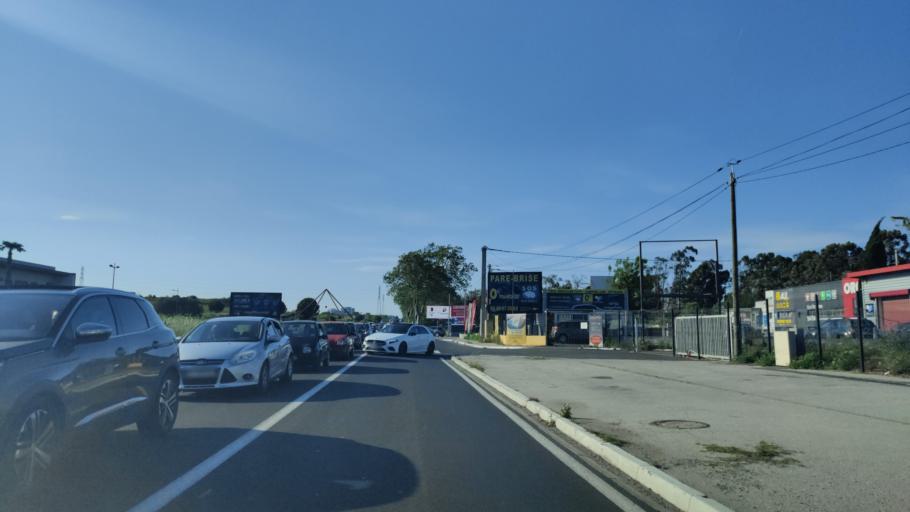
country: FR
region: Languedoc-Roussillon
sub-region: Departement des Pyrenees-Orientales
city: Cabestany
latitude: 42.6686
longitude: 2.9176
